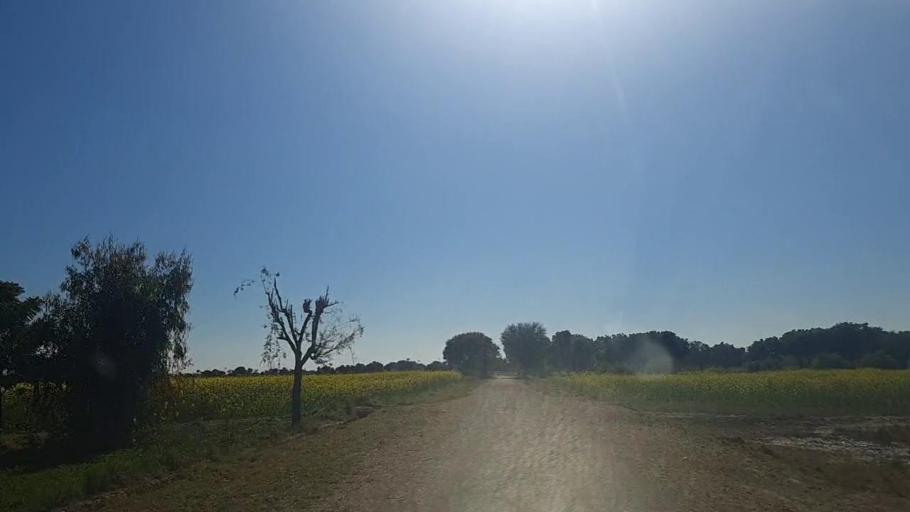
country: PK
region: Sindh
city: Sanghar
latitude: 26.1957
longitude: 68.9105
